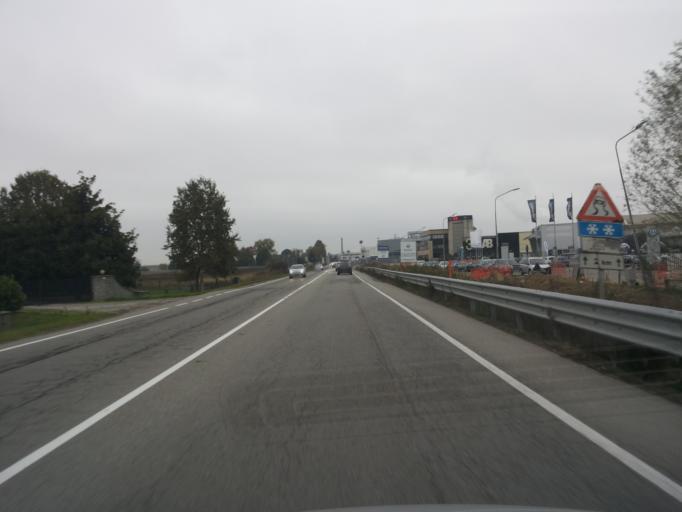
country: IT
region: Piedmont
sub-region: Provincia di Novara
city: Lumellogno
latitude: 45.4238
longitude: 8.5747
